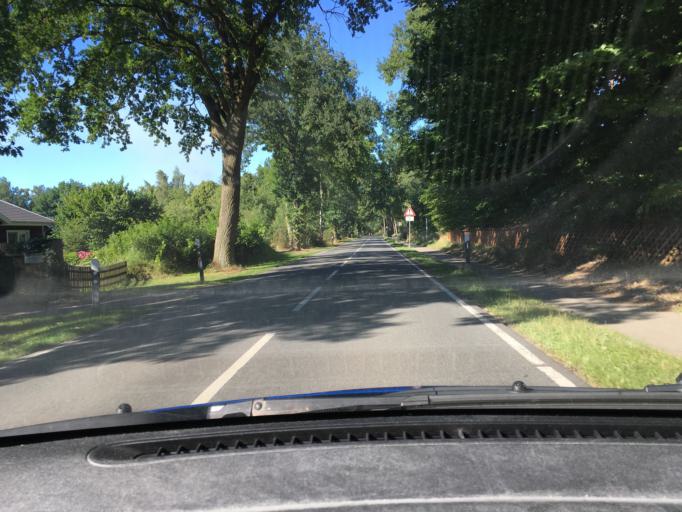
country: DE
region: Lower Saxony
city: Neetze
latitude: 53.2908
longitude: 10.6518
